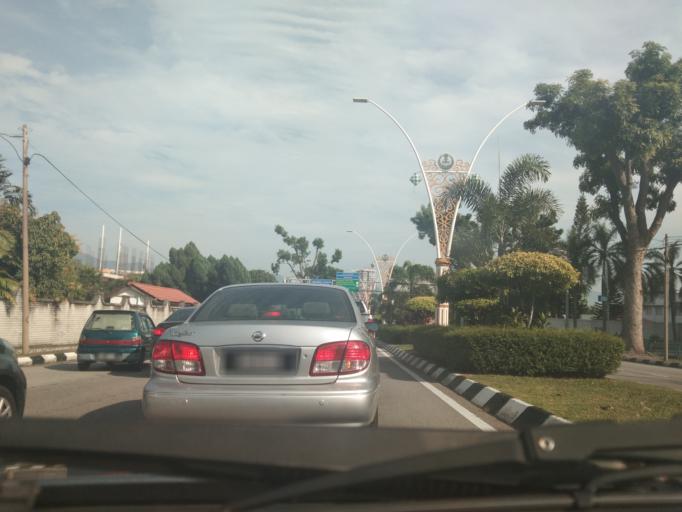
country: MY
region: Perak
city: Ipoh
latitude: 4.5904
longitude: 101.0923
